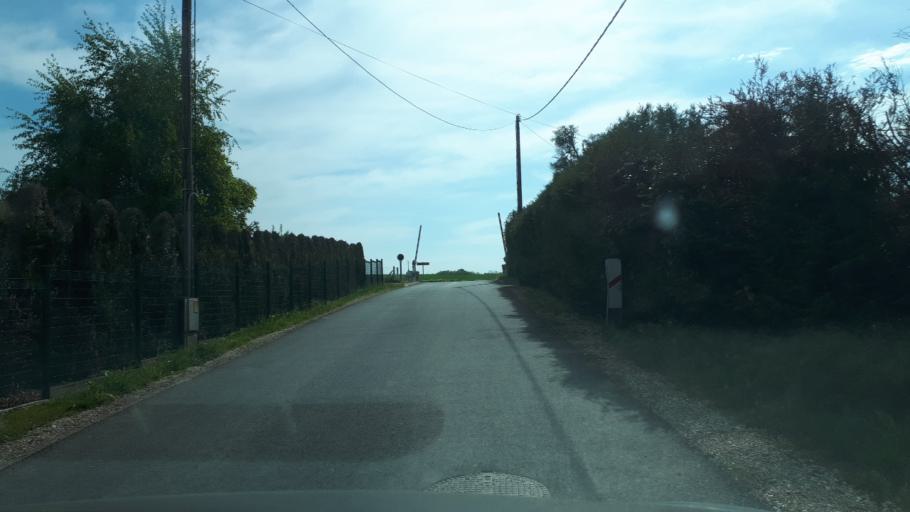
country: FR
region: Centre
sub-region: Departement du Loir-et-Cher
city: Naveil
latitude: 47.7714
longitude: 1.0166
